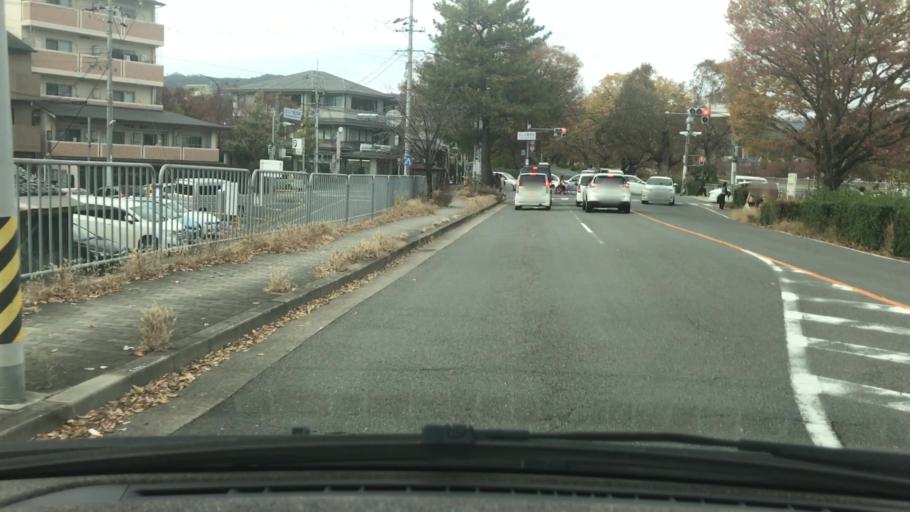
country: JP
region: Kyoto
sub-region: Kyoto-shi
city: Kamigyo-ku
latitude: 35.0496
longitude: 135.7580
